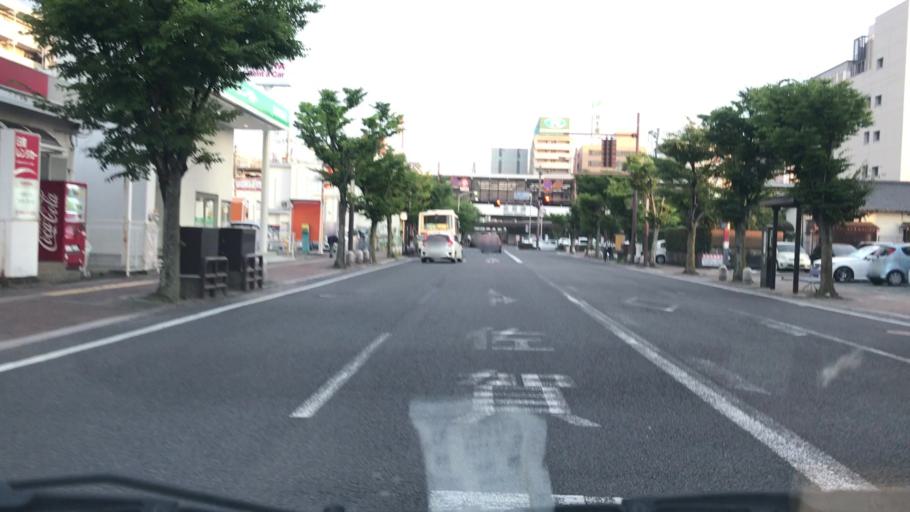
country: JP
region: Saga Prefecture
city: Saga-shi
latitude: 33.2658
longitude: 130.2972
